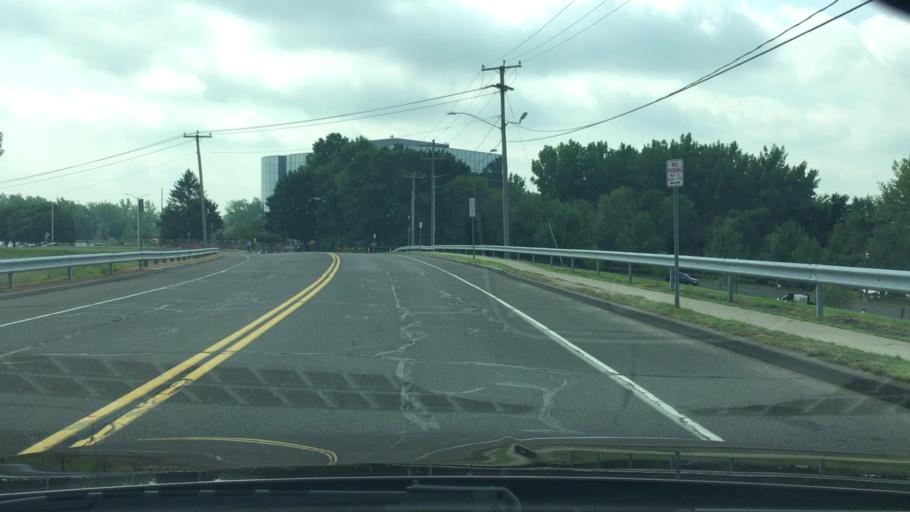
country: US
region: Connecticut
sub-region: Hartford County
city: Hartford
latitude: 41.7603
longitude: -72.6600
